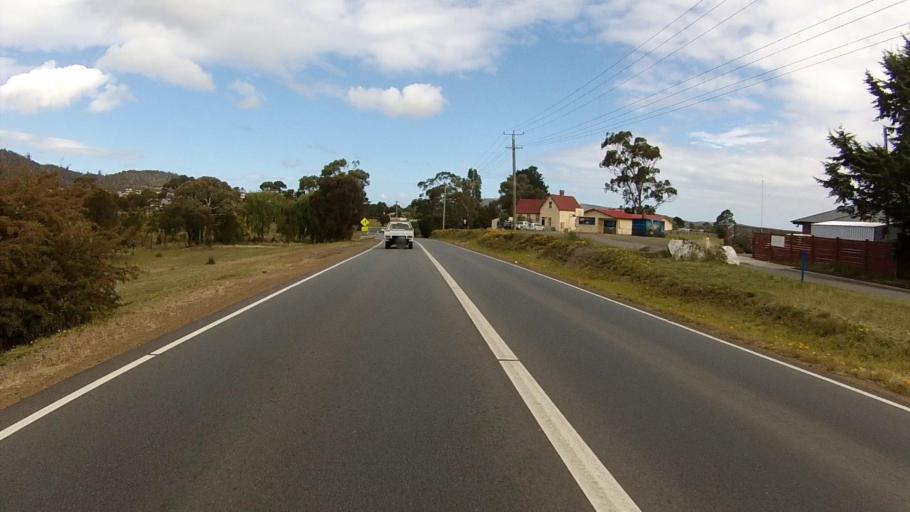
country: AU
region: Tasmania
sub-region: Clarence
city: Rokeby
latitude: -42.8975
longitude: 147.4412
